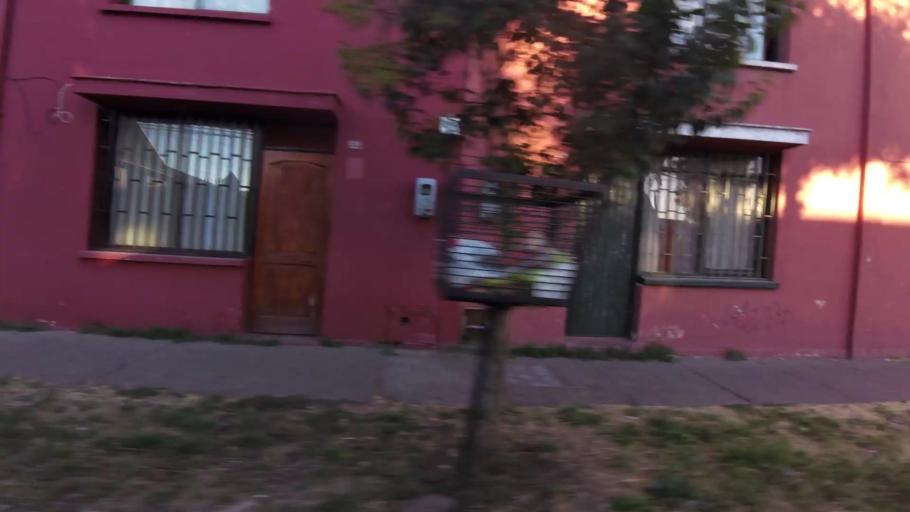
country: CL
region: Maule
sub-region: Provincia de Curico
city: Curico
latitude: -34.9960
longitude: -71.2367
